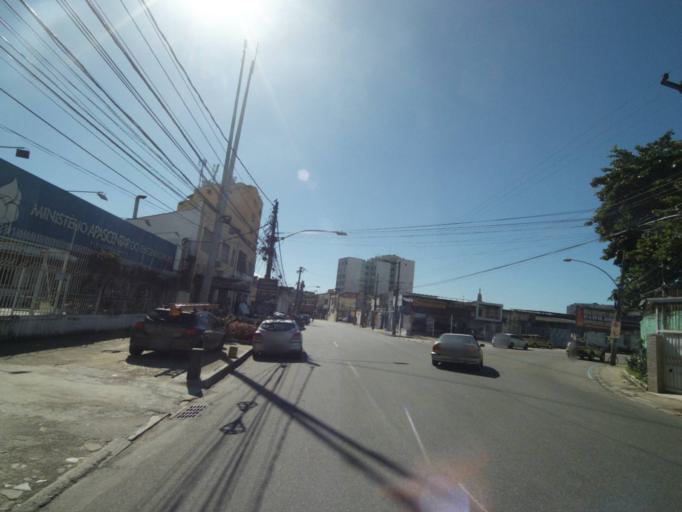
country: BR
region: Rio de Janeiro
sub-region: Rio De Janeiro
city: Rio de Janeiro
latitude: -22.9054
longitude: -43.2701
